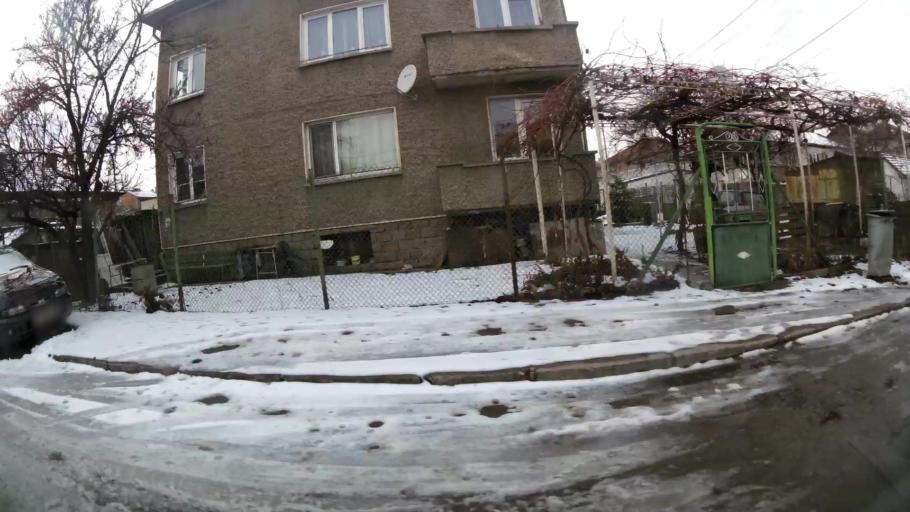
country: BG
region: Sofia-Capital
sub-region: Stolichna Obshtina
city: Sofia
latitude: 42.7281
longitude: 23.3433
